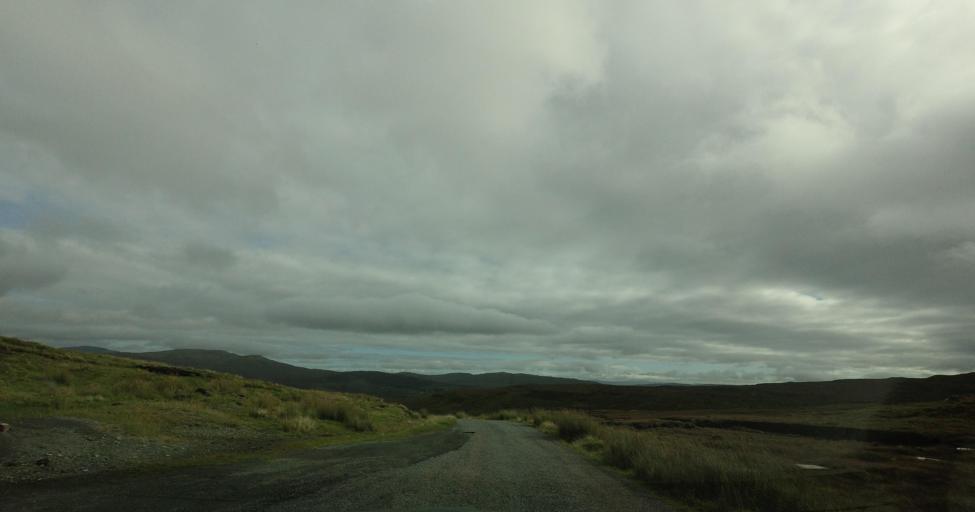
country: GB
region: Scotland
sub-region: Highland
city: Isle of Skye
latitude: 57.4112
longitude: -6.2628
